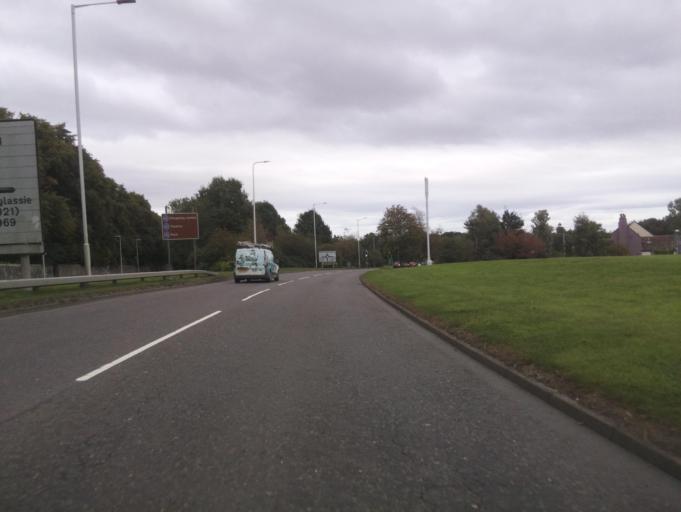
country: GB
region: Scotland
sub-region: Fife
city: Glenrothes
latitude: 56.2053
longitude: -3.1908
